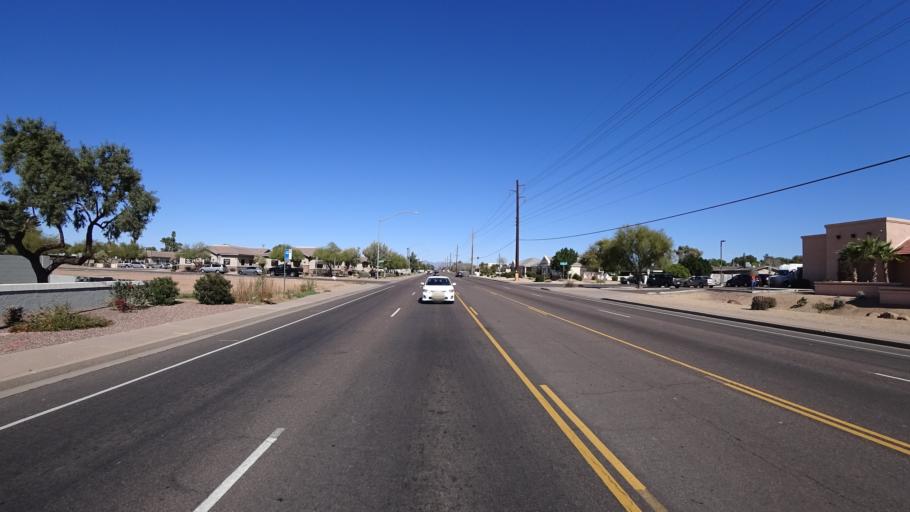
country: US
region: Arizona
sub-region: Maricopa County
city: Mesa
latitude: 33.3957
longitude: -111.8055
